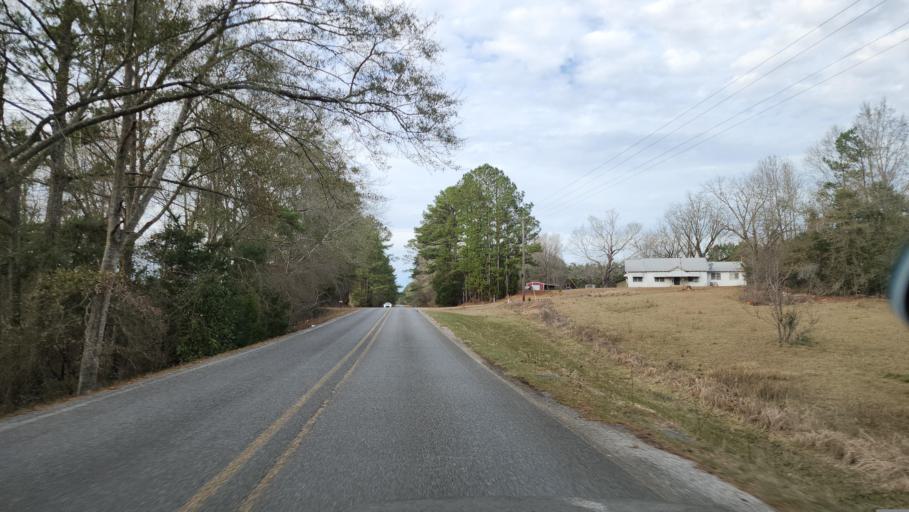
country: US
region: Mississippi
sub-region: Clarke County
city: Stonewall
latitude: 32.1900
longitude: -88.6801
